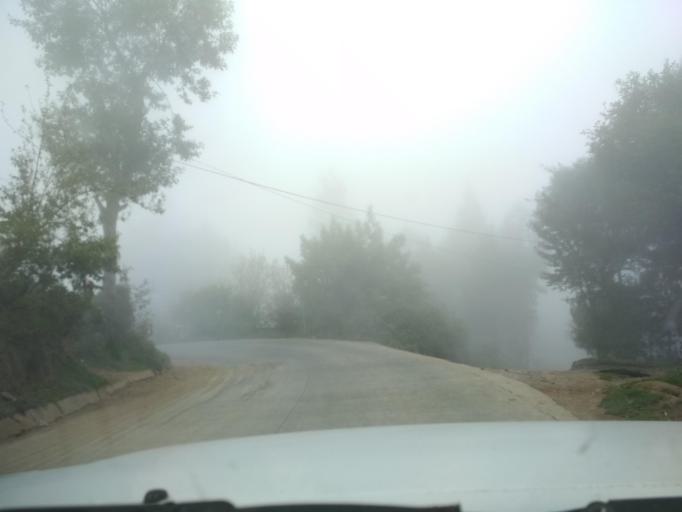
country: MX
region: Veracruz
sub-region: La Perla
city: Chilapa
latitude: 18.9779
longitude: -97.1888
